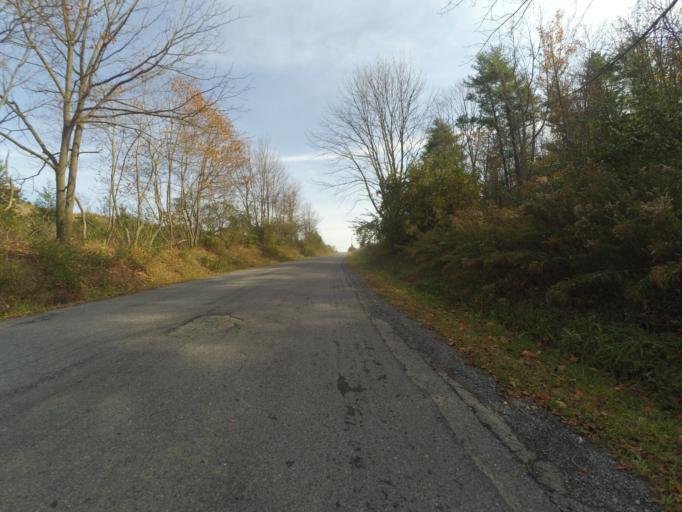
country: US
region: Pennsylvania
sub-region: Centre County
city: Park Forest Village
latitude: 40.9186
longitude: -77.9123
